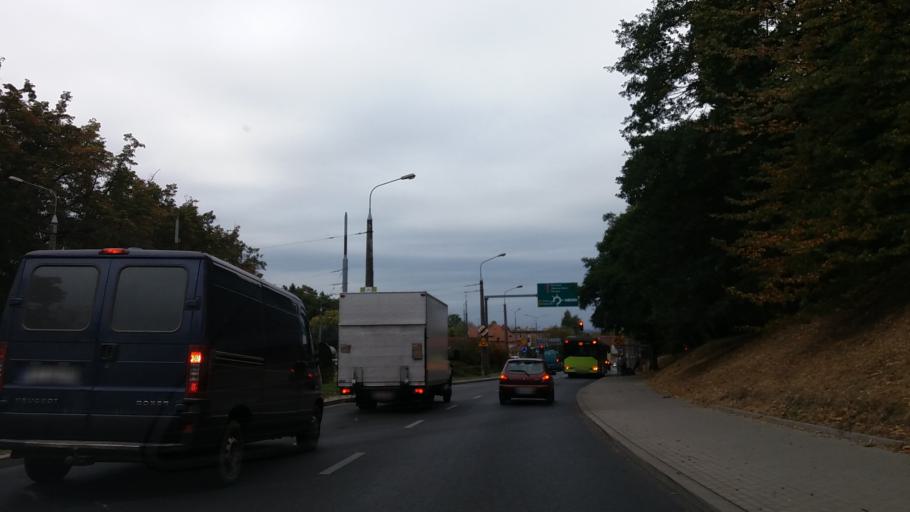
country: PL
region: Lubusz
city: Gorzow Wielkopolski
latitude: 52.7390
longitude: 15.2564
